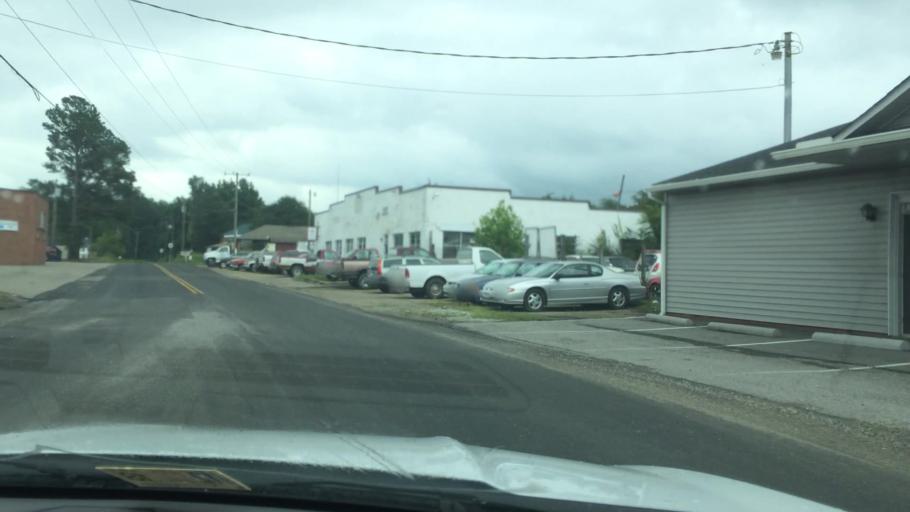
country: US
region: Virginia
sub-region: New Kent County
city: New Kent
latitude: 37.4418
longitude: -77.0439
